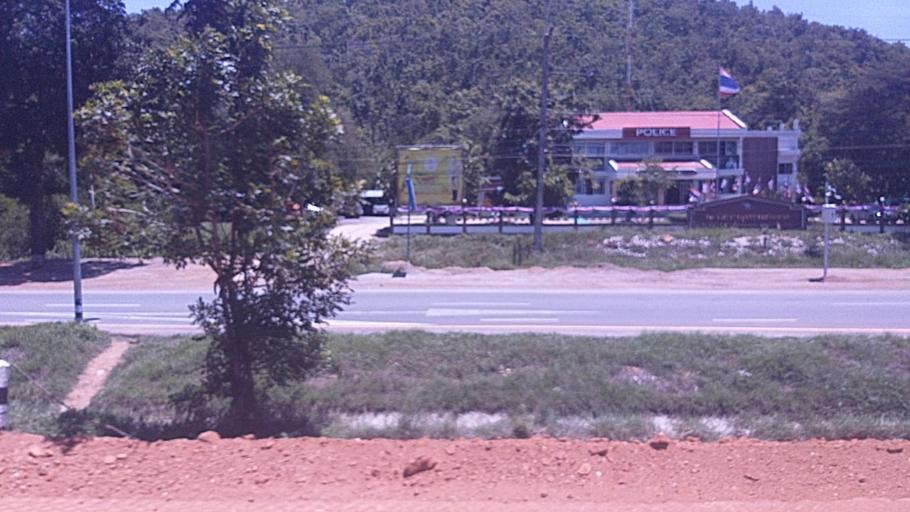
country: TH
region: Chaiyaphum
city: Kaeng Khro
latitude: 16.0643
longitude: 102.2762
